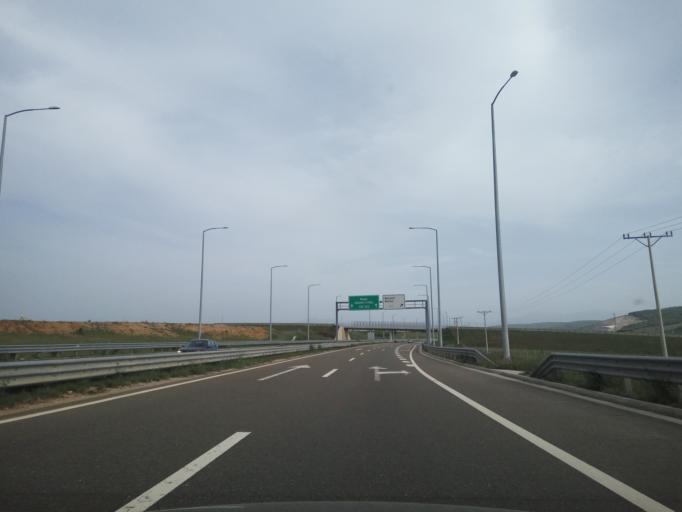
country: XK
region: Prizren
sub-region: Komuna e Therandes
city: Nishor
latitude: 42.4715
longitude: 20.8027
